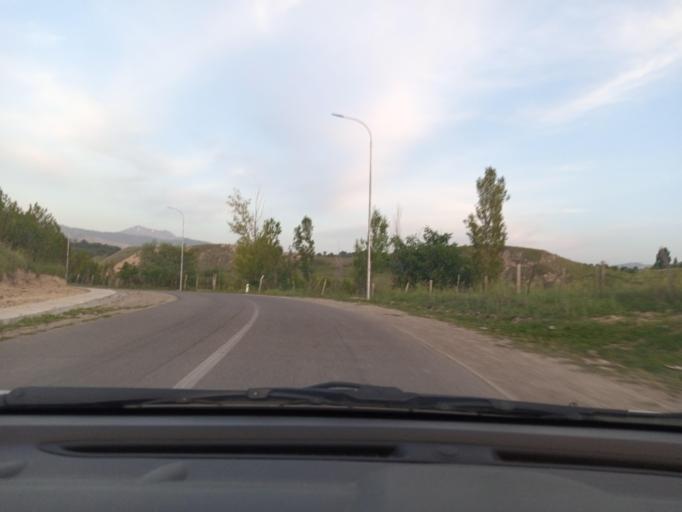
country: UZ
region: Toshkent
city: Parkent
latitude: 41.2454
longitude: 69.7421
